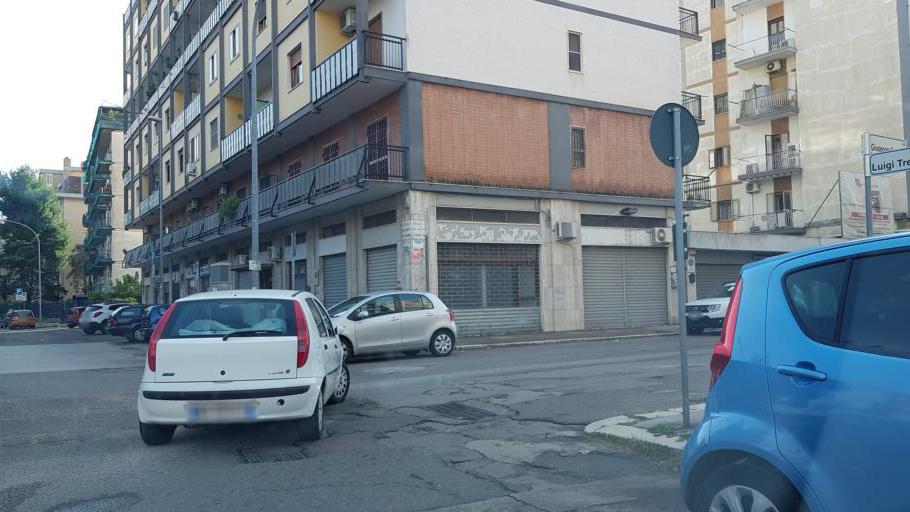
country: IT
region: Apulia
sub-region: Provincia di Foggia
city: Foggia
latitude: 41.4550
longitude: 15.5623
